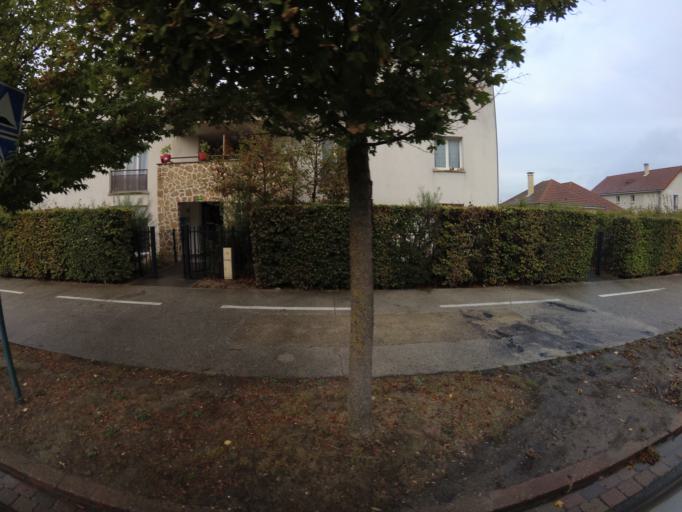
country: FR
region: Ile-de-France
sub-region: Departement de Seine-et-Marne
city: Chanteloup-en-Brie
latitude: 48.8609
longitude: 2.7395
